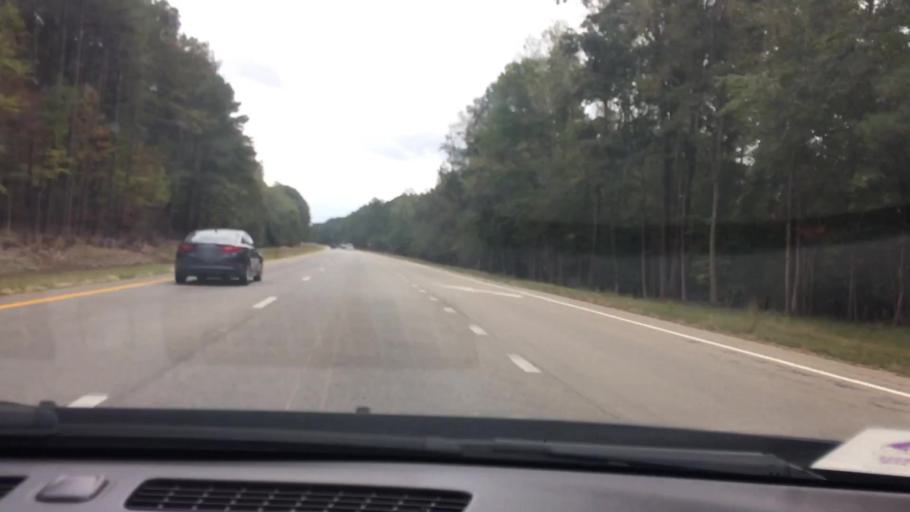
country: US
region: North Carolina
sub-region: Wake County
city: Zebulon
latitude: 35.7974
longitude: -78.1854
